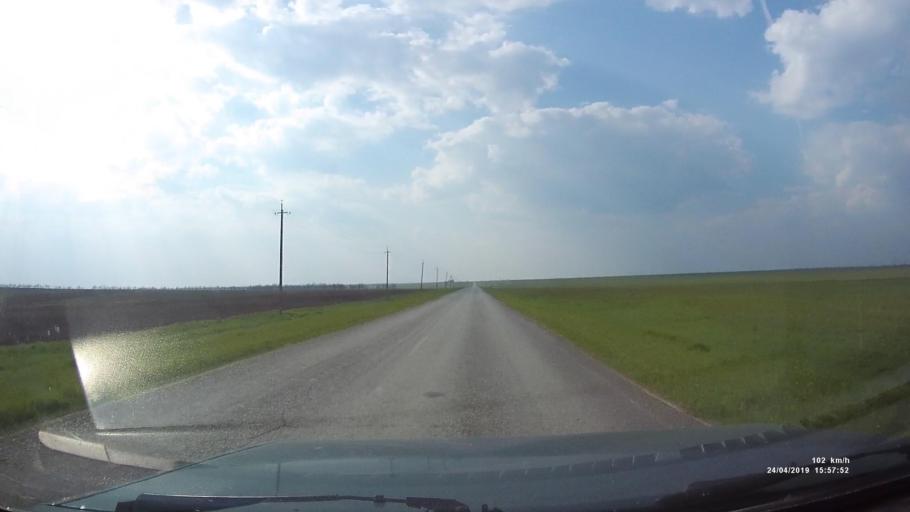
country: RU
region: Kalmykiya
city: Yashalta
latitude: 46.6089
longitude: 42.5006
